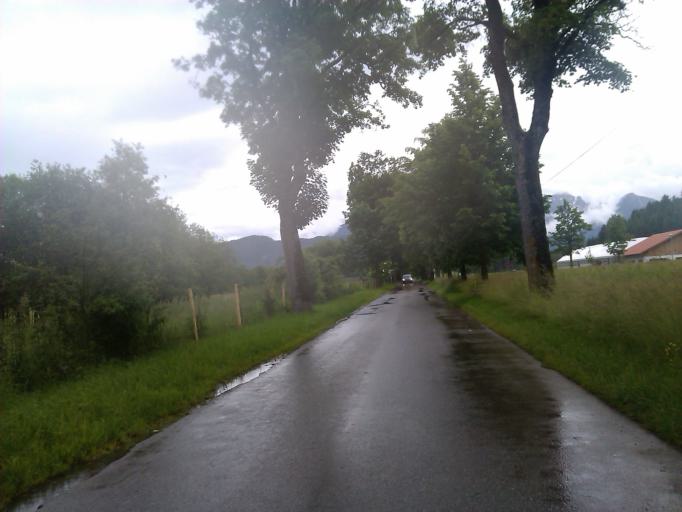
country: DE
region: Bavaria
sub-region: Swabia
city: Fuessen
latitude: 47.5984
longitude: 10.7130
